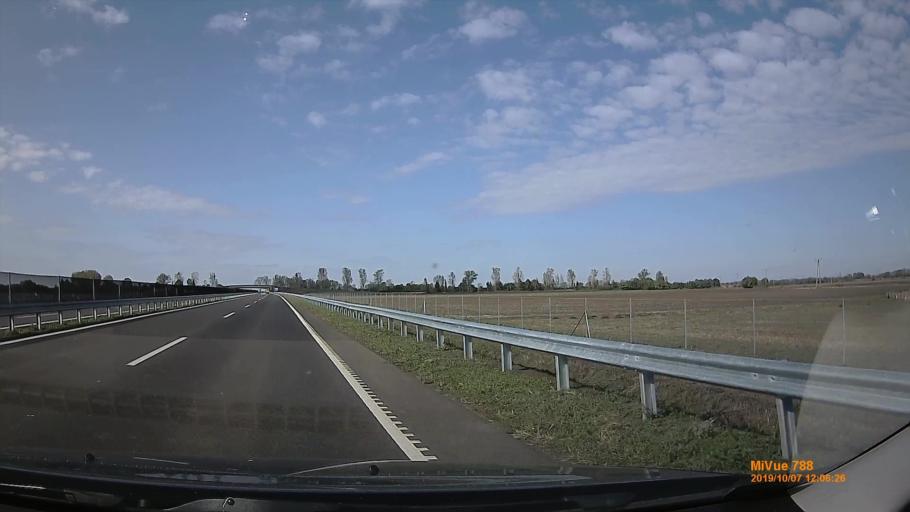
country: HU
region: Bekes
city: Bekesszentandras
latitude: 46.8236
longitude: 20.4985
